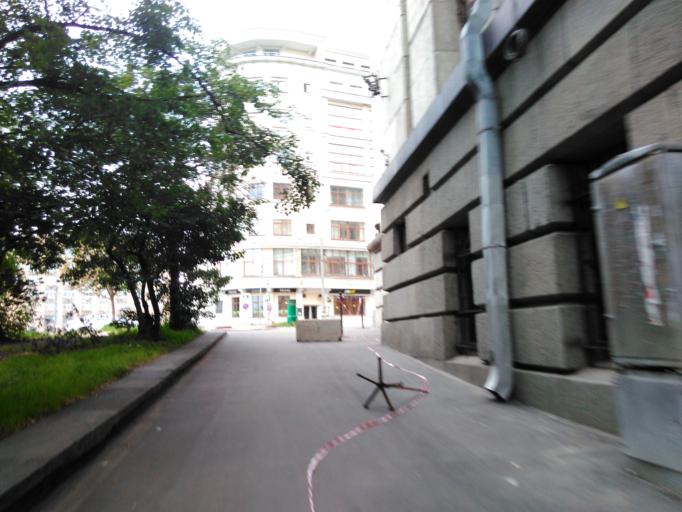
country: RU
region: Moscow
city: Lefortovo
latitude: 55.7632
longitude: 37.6842
